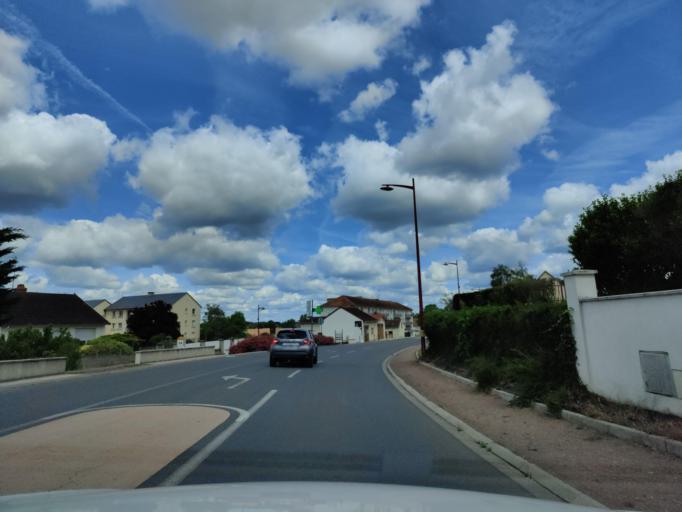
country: FR
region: Auvergne
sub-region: Departement de l'Allier
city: Saint-Victor
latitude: 46.3949
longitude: 2.6094
